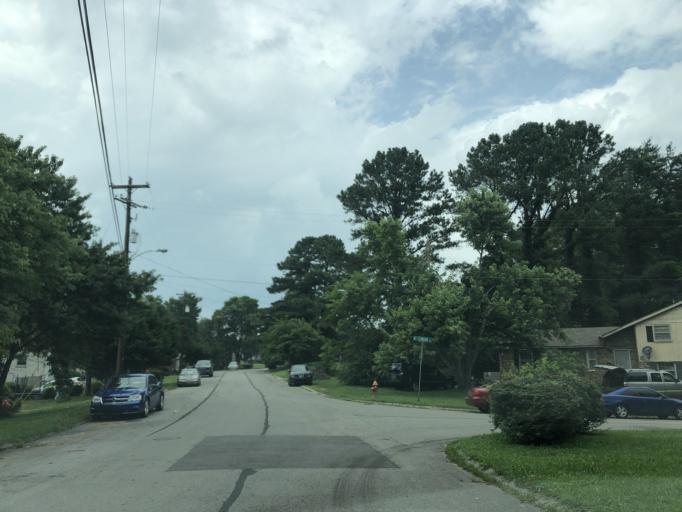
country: US
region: Tennessee
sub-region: Williamson County
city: Brentwood Estates
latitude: 36.0556
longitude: -86.6890
